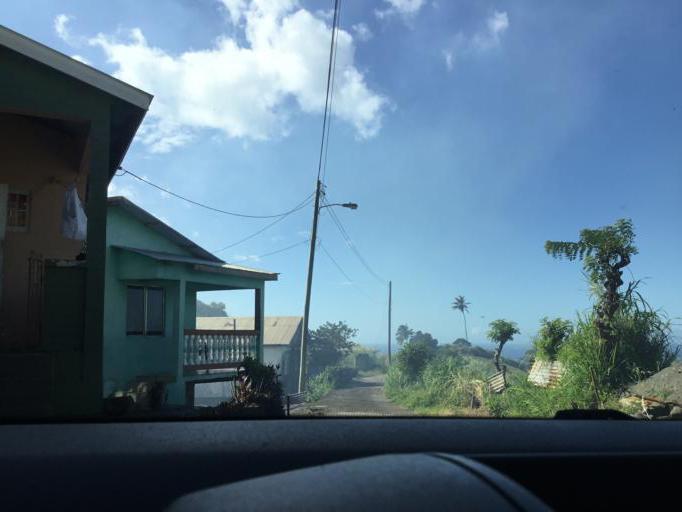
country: VC
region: Saint David
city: Chateaubelair
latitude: 13.2703
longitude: -61.2418
